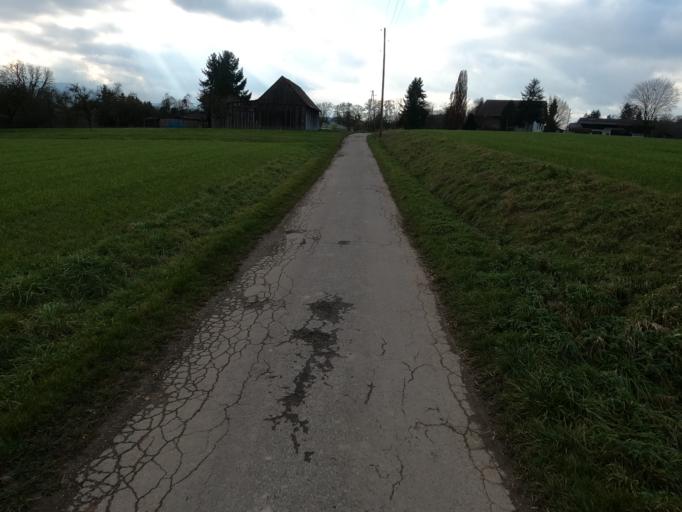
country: DE
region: Baden-Wuerttemberg
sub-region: Regierungsbezirk Stuttgart
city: Heiningen
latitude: 48.6820
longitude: 9.6179
